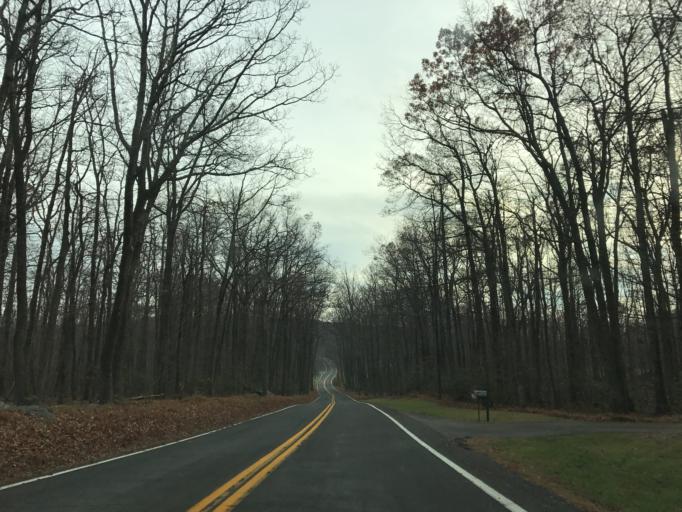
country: US
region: Maryland
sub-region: Frederick County
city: Myersville
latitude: 39.5519
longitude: -77.5008
